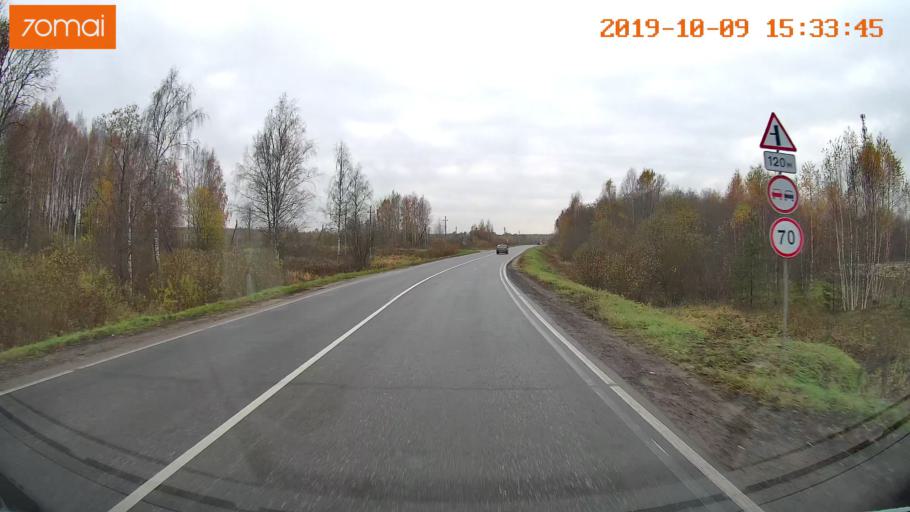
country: RU
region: Kostroma
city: Oktyabr'skiy
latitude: 57.9477
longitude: 41.2579
